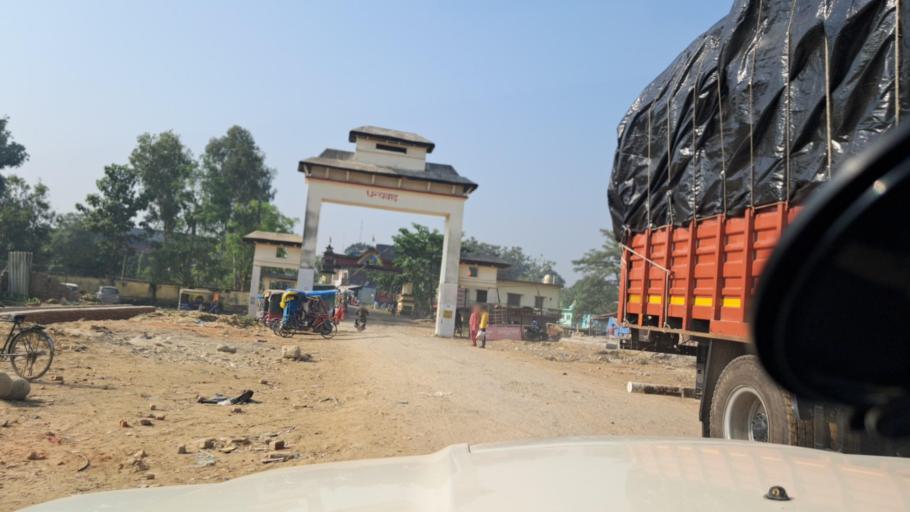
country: IN
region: Uttar Pradesh
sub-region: Maharajganj
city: Nichlaul
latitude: 27.4333
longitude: 83.6949
